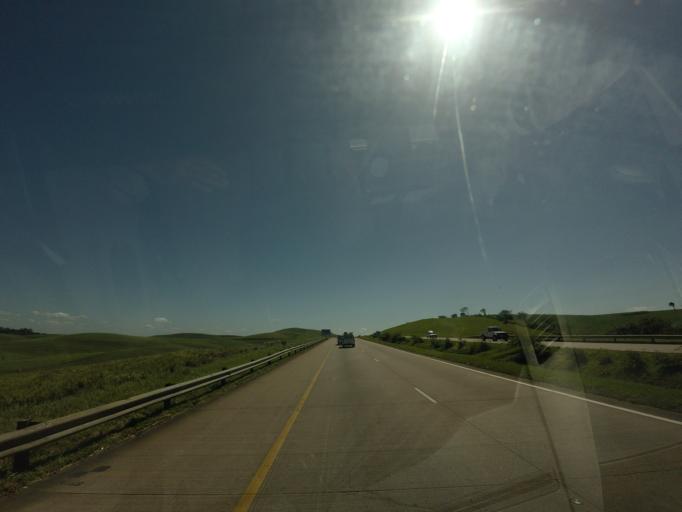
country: ZA
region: KwaZulu-Natal
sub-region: iLembe District Municipality
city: Ballitoville
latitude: -29.4422
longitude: 31.2580
